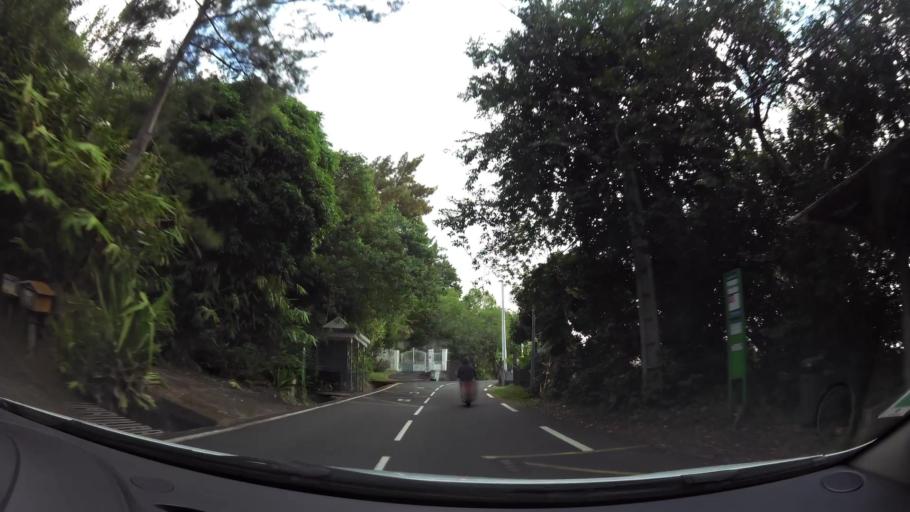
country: RE
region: Reunion
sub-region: Reunion
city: Saint-Denis
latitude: -20.9086
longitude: 55.4431
